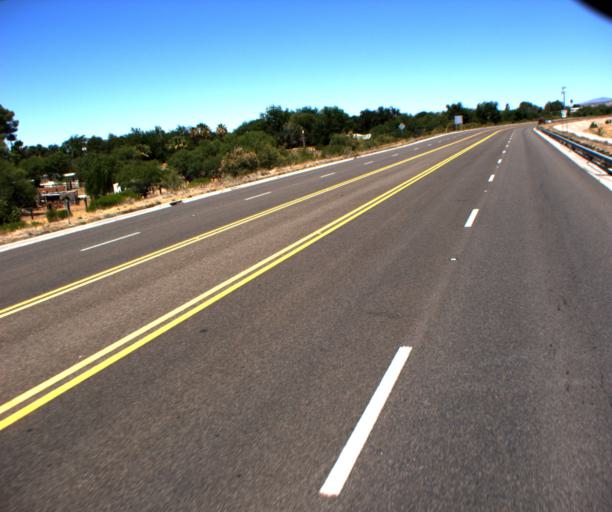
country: US
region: Arizona
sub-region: Maricopa County
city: Wickenburg
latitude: 33.9739
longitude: -112.7307
